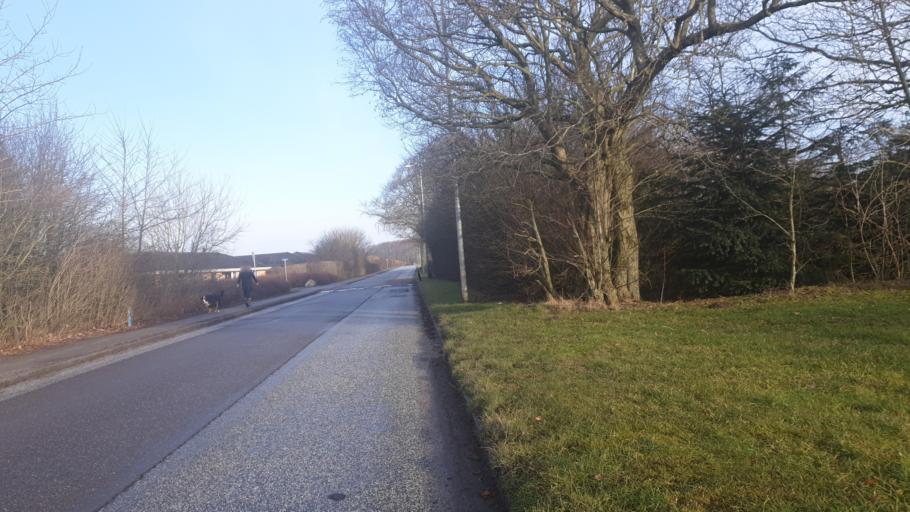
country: DK
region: Central Jutland
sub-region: Hedensted Kommune
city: Hedensted
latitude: 55.7681
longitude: 9.7209
